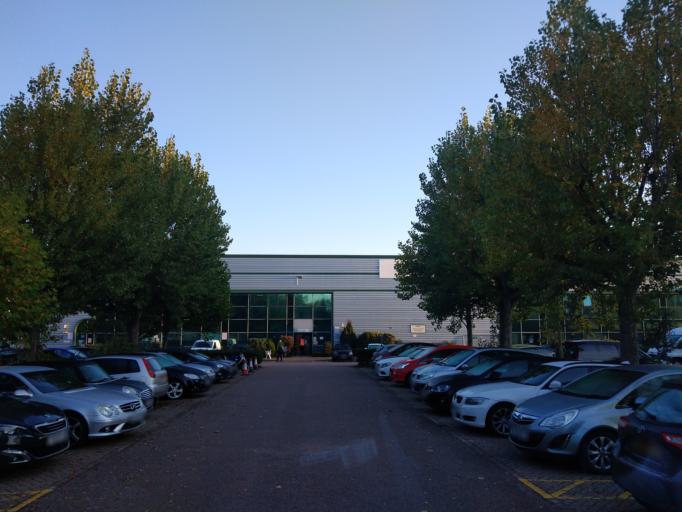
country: GB
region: England
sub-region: West Sussex
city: Littlehampton
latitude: 50.8213
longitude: -0.5288
